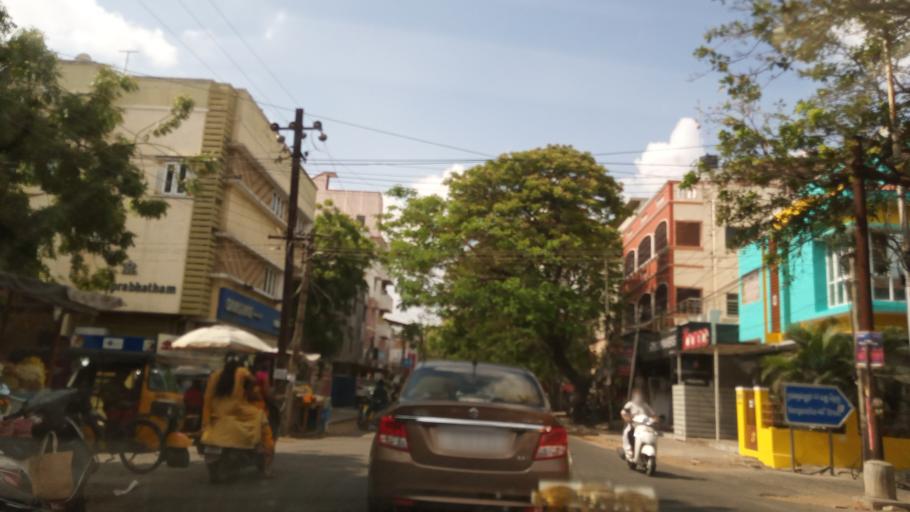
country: IN
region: Tamil Nadu
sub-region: Kancheepuram
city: Madipakkam
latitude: 12.9821
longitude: 80.1884
